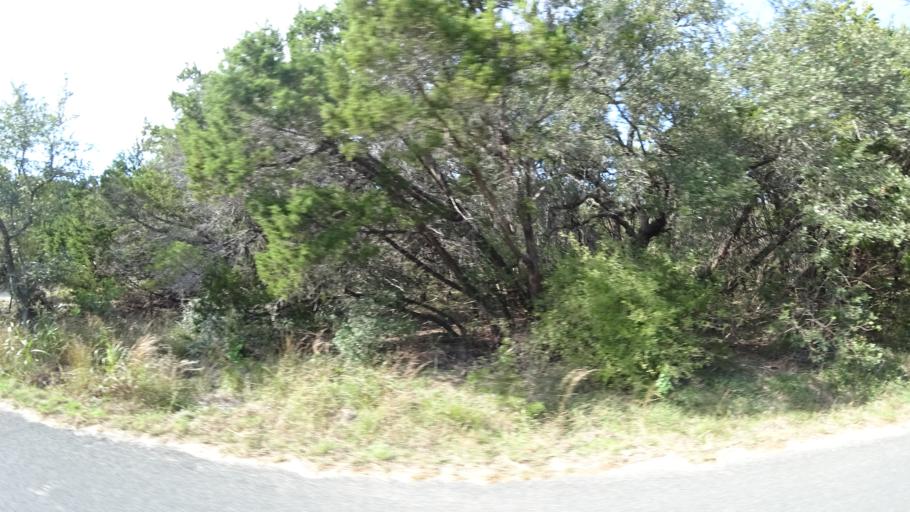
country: US
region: Texas
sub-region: Travis County
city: Shady Hollow
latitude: 30.2210
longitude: -97.9298
